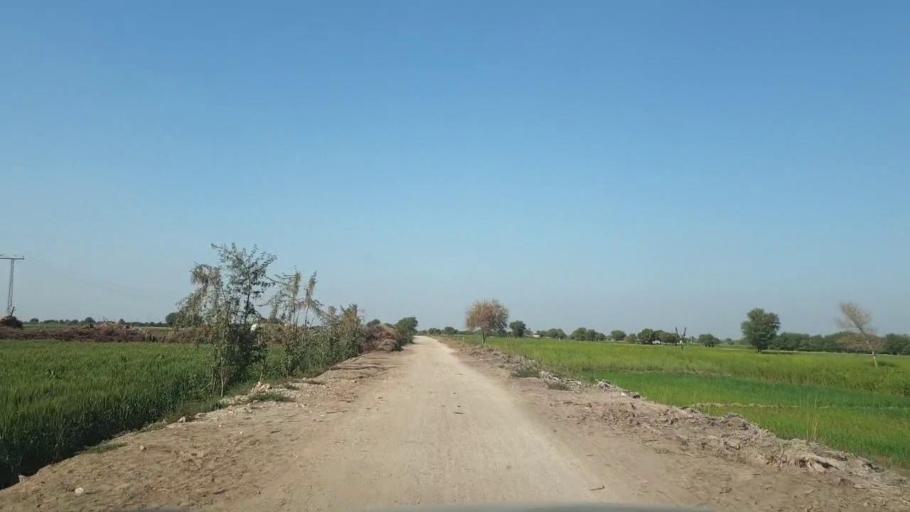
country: PK
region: Sindh
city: Tando Adam
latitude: 25.6631
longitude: 68.6933
